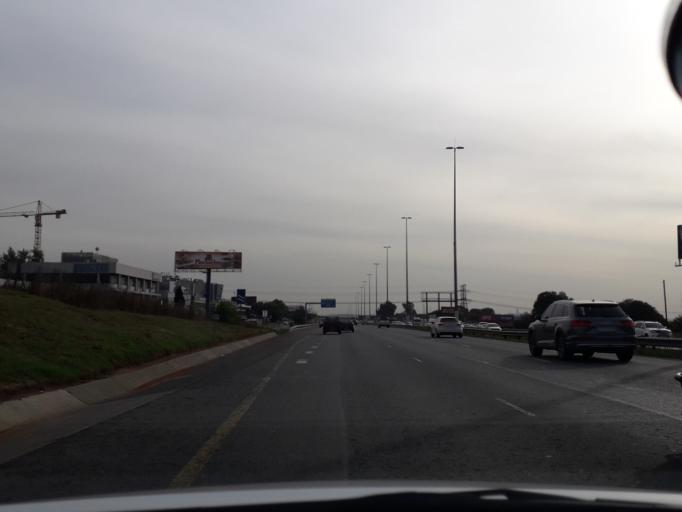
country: ZA
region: Gauteng
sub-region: City of Johannesburg Metropolitan Municipality
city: Modderfontein
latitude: -26.1345
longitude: 28.2005
